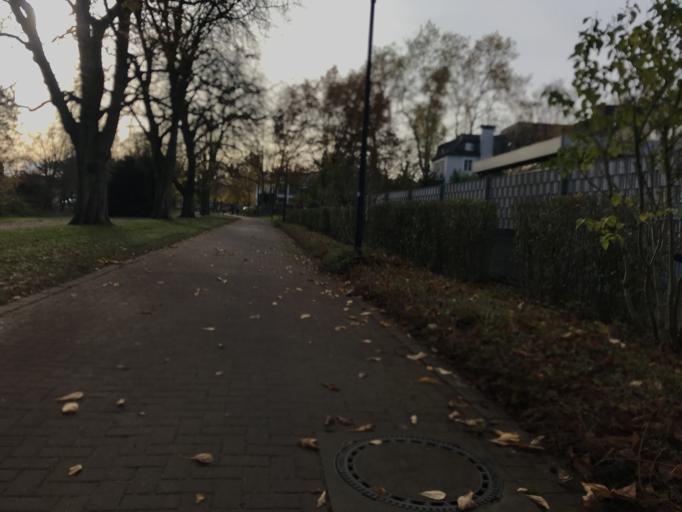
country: DE
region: North Rhine-Westphalia
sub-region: Regierungsbezirk Arnsberg
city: Hamm
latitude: 51.6810
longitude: 7.8255
